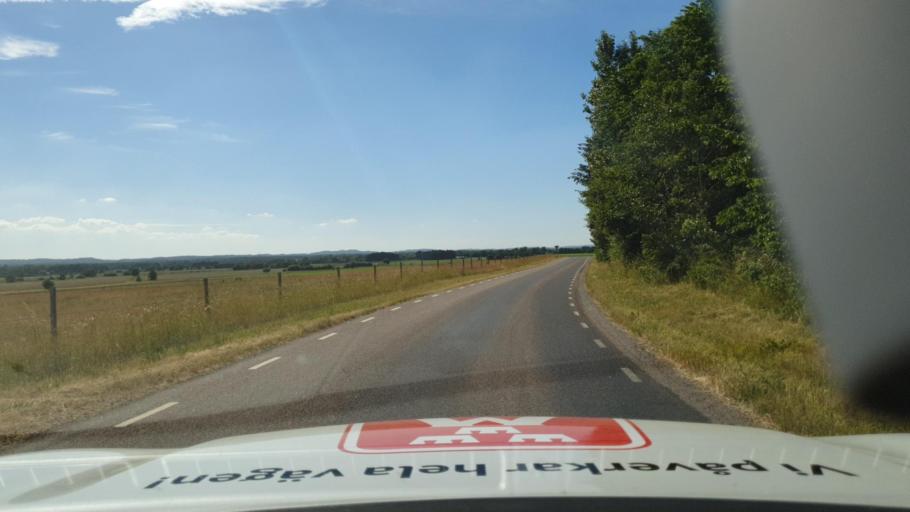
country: SE
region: Skane
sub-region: Sjobo Kommun
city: Sjoebo
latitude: 55.6186
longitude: 13.6530
